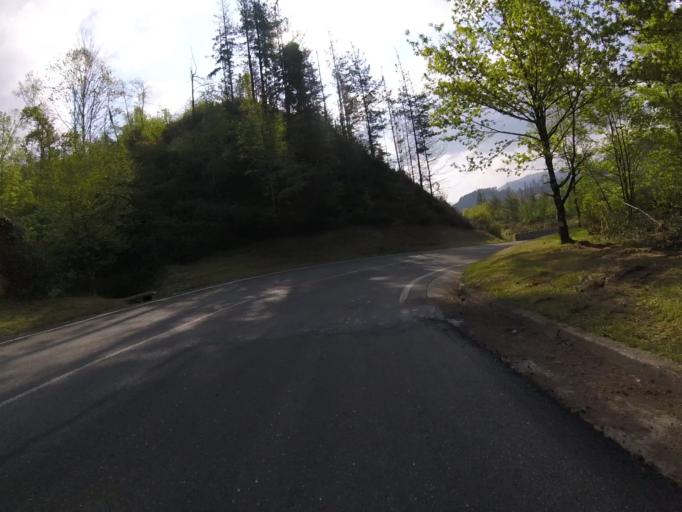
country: ES
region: Basque Country
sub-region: Provincia de Guipuzcoa
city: Azkoitia
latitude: 43.2028
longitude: -2.3544
